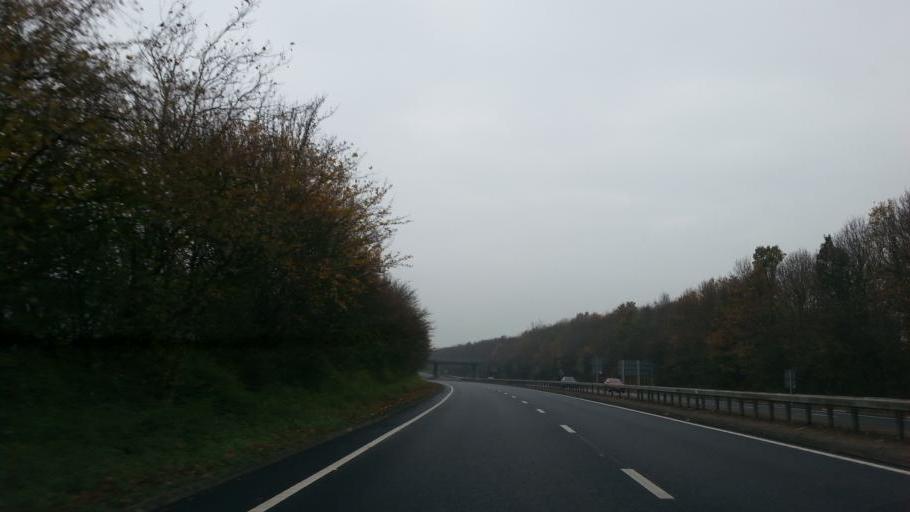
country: GB
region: England
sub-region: Cambridgeshire
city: Yaxley
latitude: 52.5393
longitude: -0.3035
